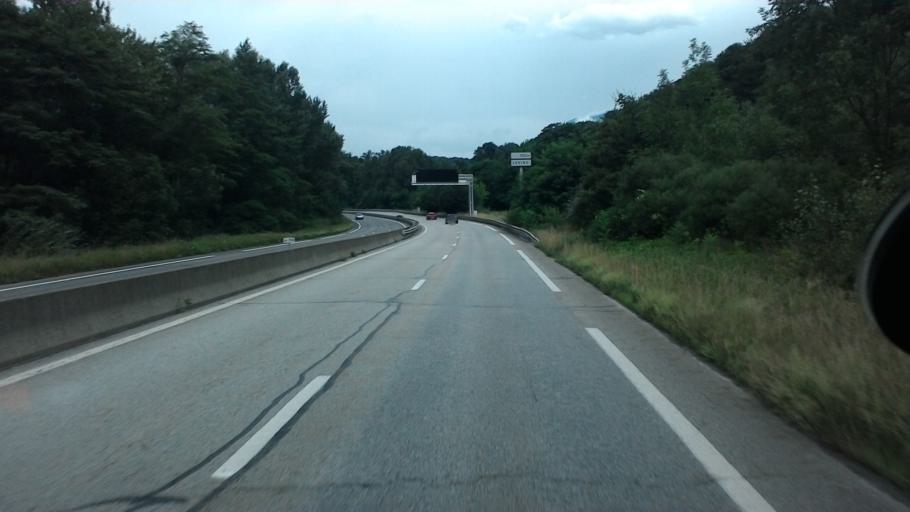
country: FR
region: Rhone-Alpes
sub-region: Departement de la Savoie
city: La Bathie
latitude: 45.5796
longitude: 6.4596
